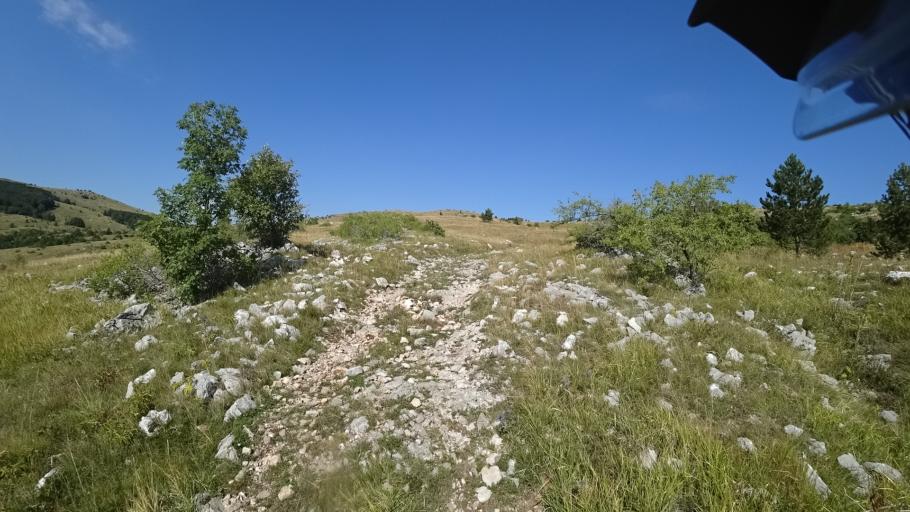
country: HR
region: Zadarska
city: Gracac
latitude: 44.3075
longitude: 16.0004
